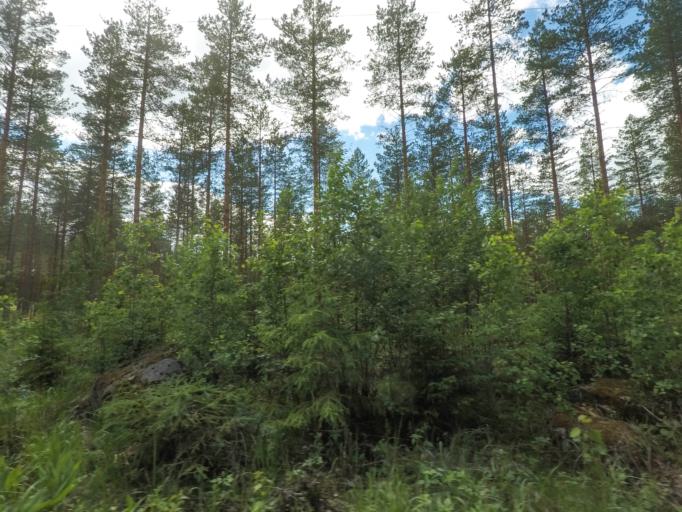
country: FI
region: Central Finland
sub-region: Jyvaeskylae
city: Hankasalmi
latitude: 62.4088
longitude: 26.6502
